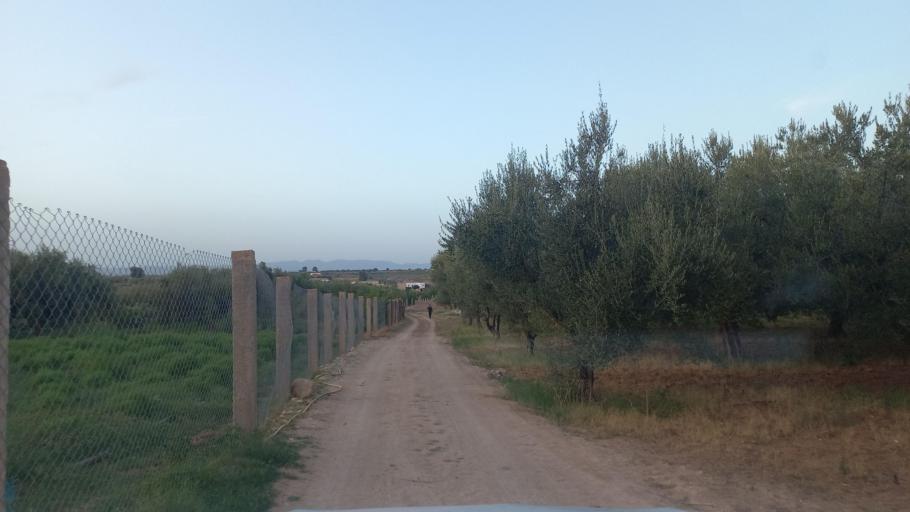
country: TN
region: Al Qasrayn
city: Kasserine
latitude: 35.2164
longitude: 9.0525
